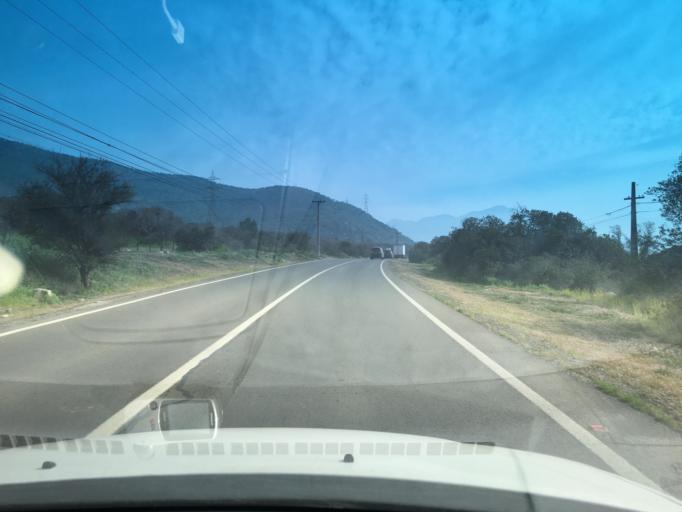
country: CL
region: Santiago Metropolitan
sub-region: Provincia de Chacabuco
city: Lampa
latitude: -33.1490
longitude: -70.9115
